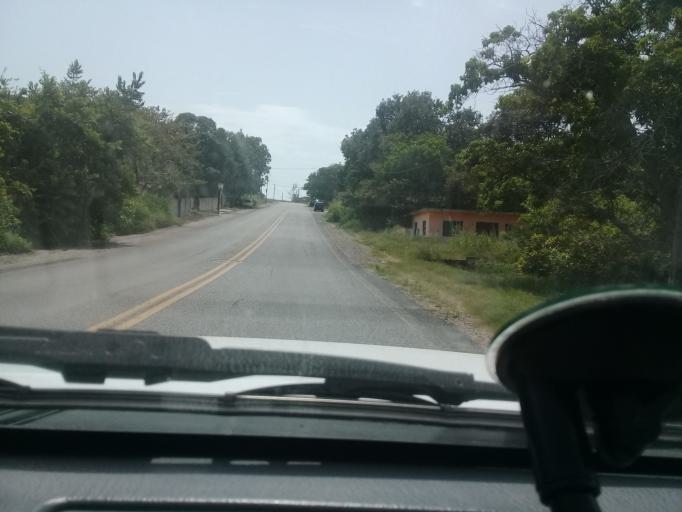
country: MX
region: Veracruz
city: Villa Cuauhtemoc
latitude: 22.2126
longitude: -97.8265
